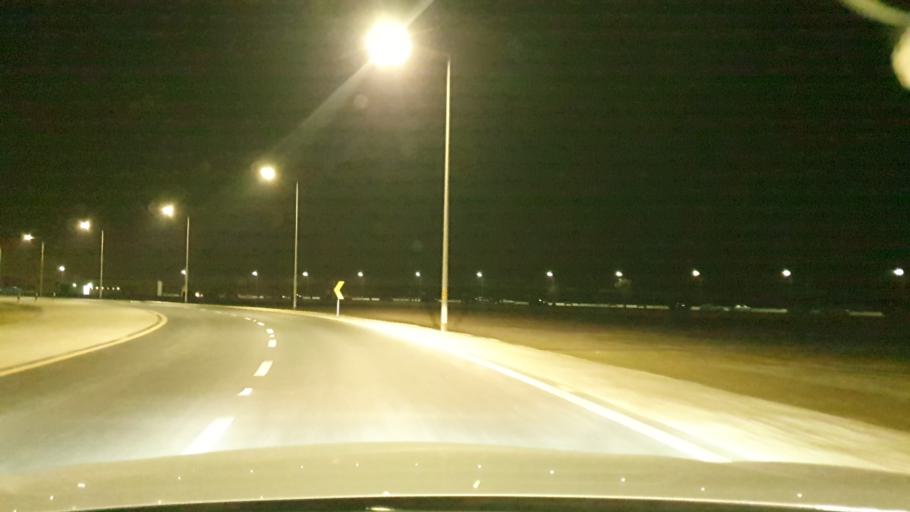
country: BH
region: Muharraq
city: Al Muharraq
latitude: 26.2854
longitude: 50.5795
